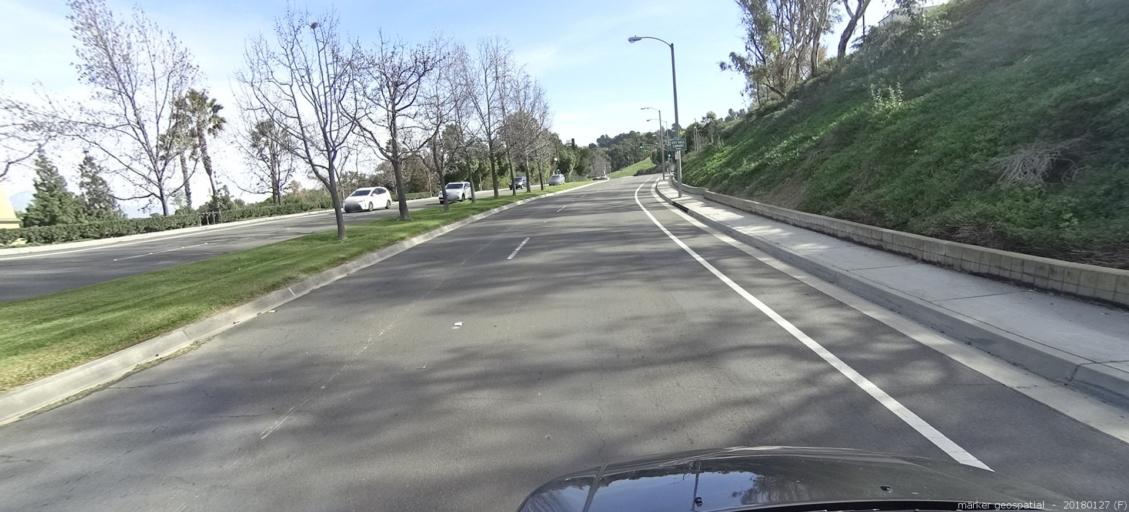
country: US
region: California
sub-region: Los Angeles County
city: Diamond Bar
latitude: 34.0027
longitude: -117.8295
